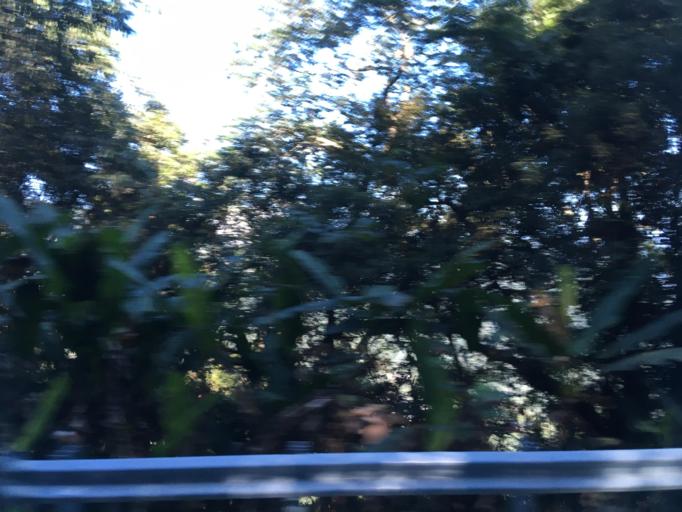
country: TW
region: Taiwan
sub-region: Chiayi
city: Jiayi Shi
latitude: 23.4116
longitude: 120.6533
